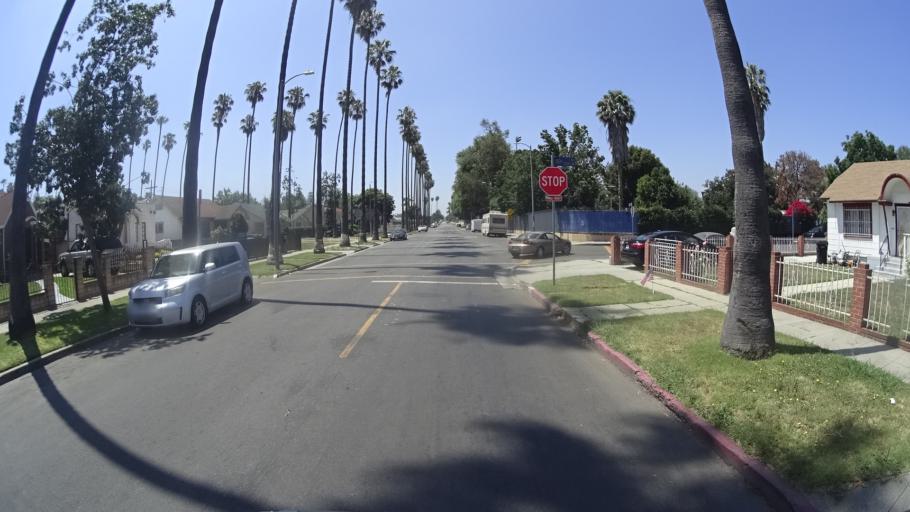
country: US
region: California
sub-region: Los Angeles County
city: View Park-Windsor Hills
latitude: 33.9984
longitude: -118.3258
